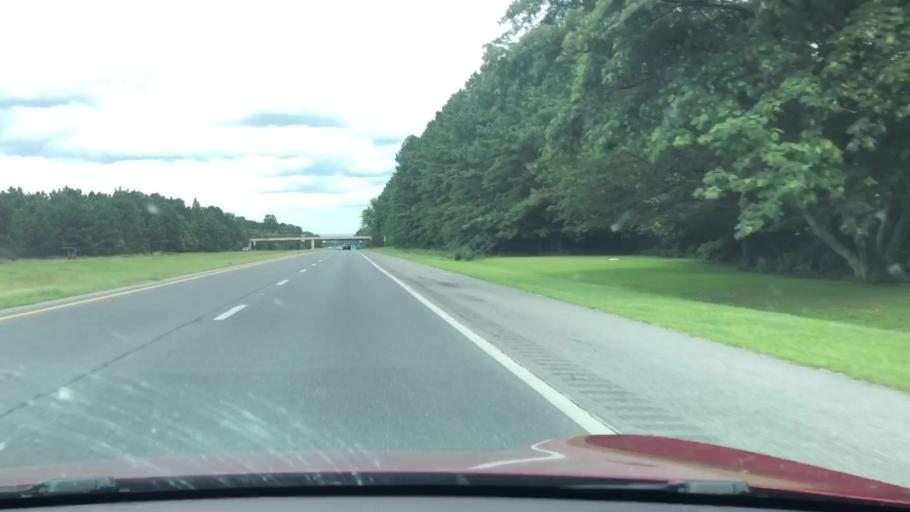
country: US
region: Maryland
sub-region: Wicomico County
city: Fruitland
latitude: 38.3180
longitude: -75.5889
